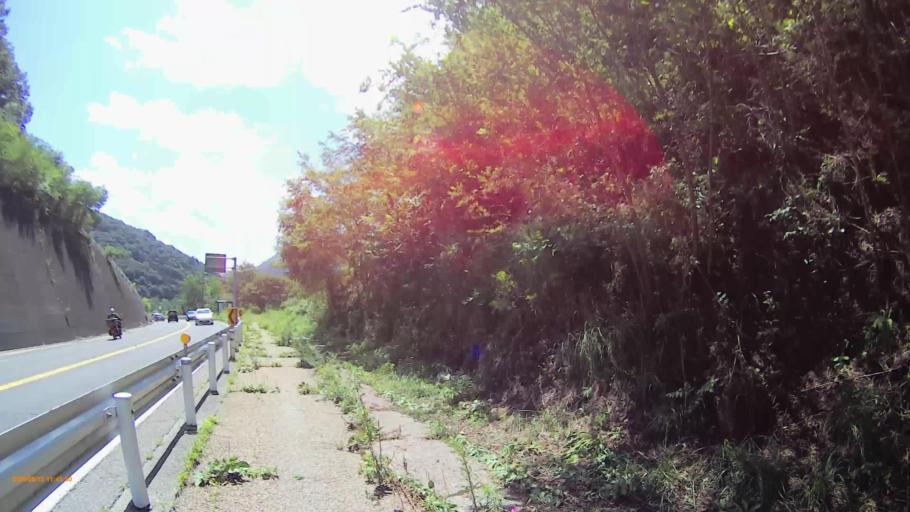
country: JP
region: Nagano
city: Ina
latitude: 35.8308
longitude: 137.6821
